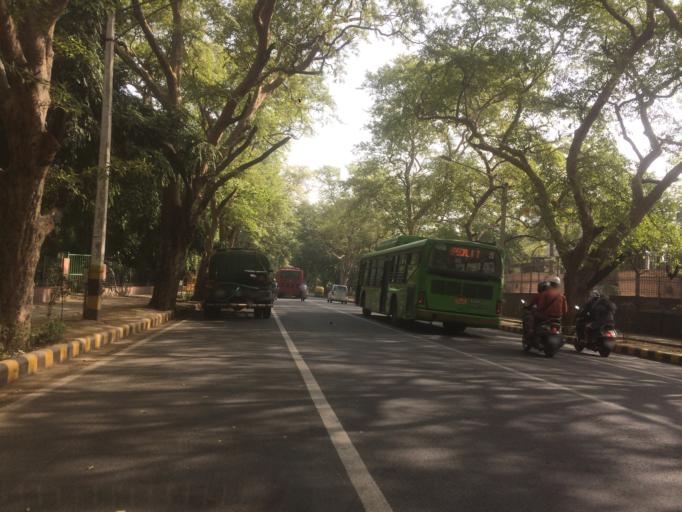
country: IN
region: NCT
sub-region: New Delhi
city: New Delhi
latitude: 28.6241
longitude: 77.1979
